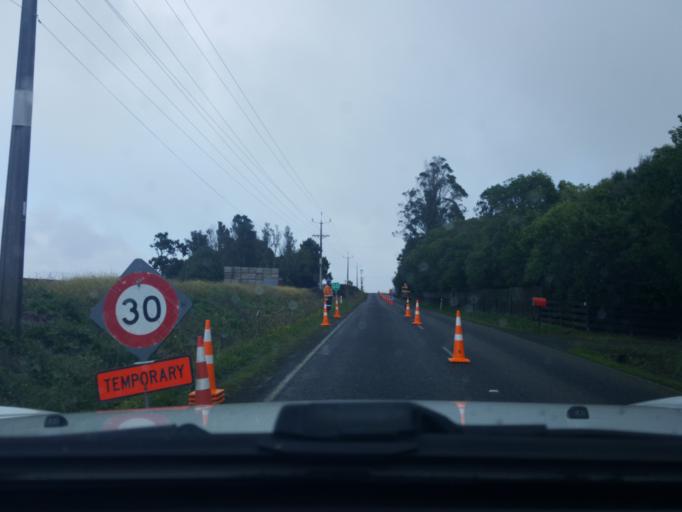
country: NZ
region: Auckland
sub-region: Auckland
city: Pukekohe East
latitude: -37.3091
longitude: 174.9916
